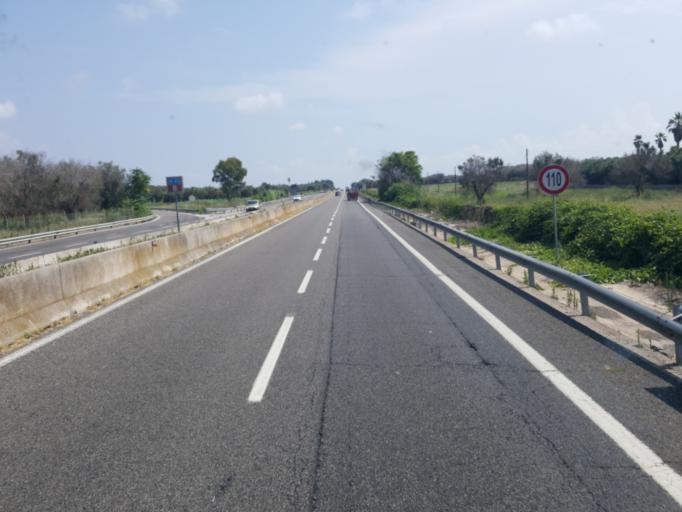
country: IT
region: Apulia
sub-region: Provincia di Brindisi
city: Torchiarolo
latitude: 40.4868
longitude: 18.0405
